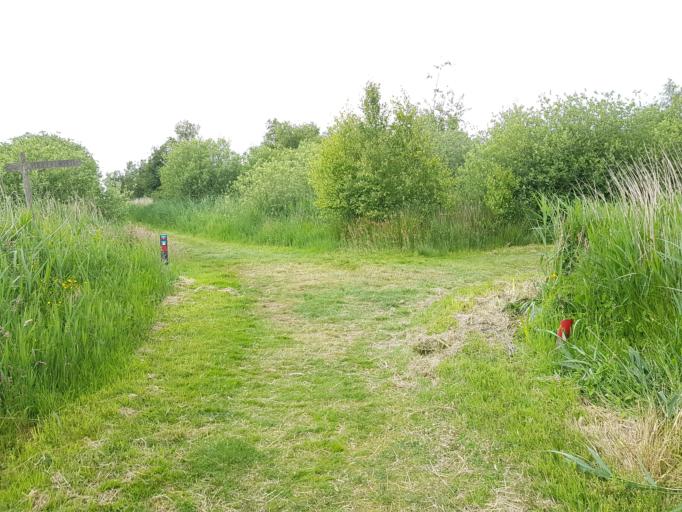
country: NL
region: Friesland
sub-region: Gemeente Tytsjerksteradiel
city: Garyp
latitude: 53.1409
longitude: 5.9504
